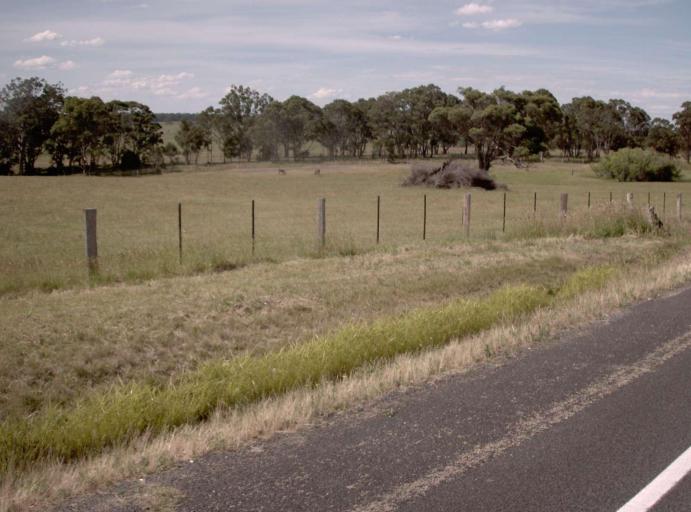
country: AU
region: Victoria
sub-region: East Gippsland
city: Lakes Entrance
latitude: -37.8197
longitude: 147.8114
